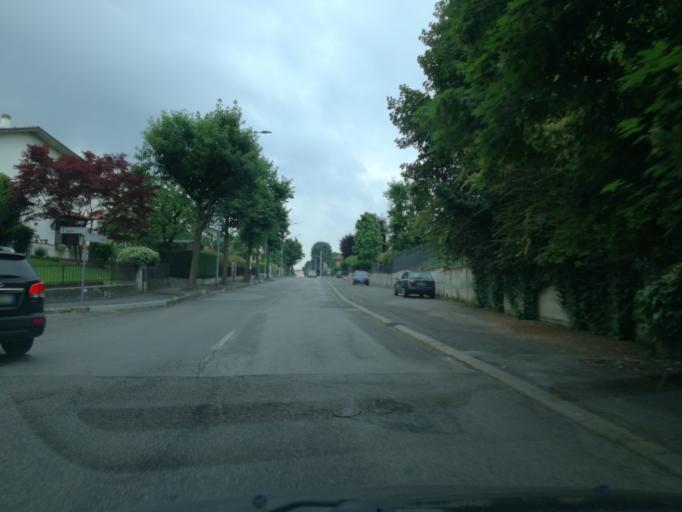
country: IT
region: Lombardy
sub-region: Provincia di Monza e Brianza
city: Carnate
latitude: 45.6488
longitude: 9.3751
